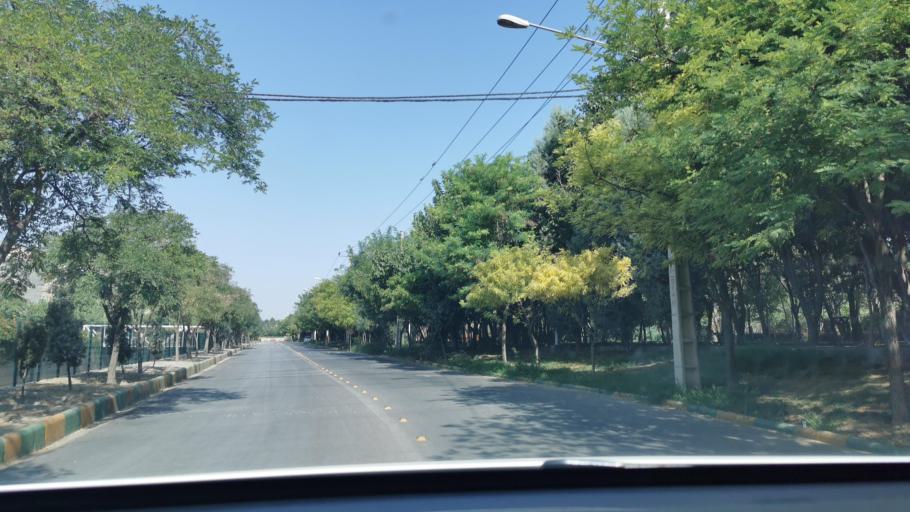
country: IR
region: Razavi Khorasan
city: Mashhad
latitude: 36.3300
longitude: 59.6345
